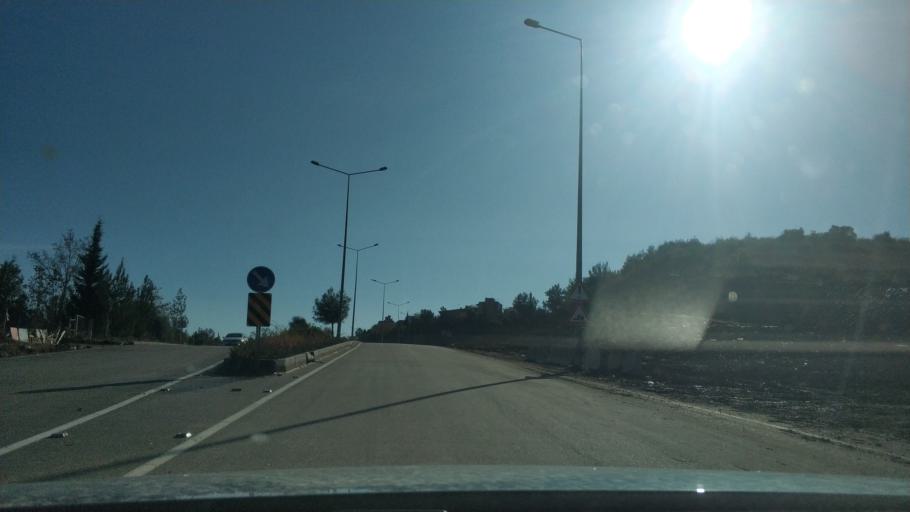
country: TR
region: Adana
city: Seyhan
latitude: 37.0656
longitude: 35.2694
